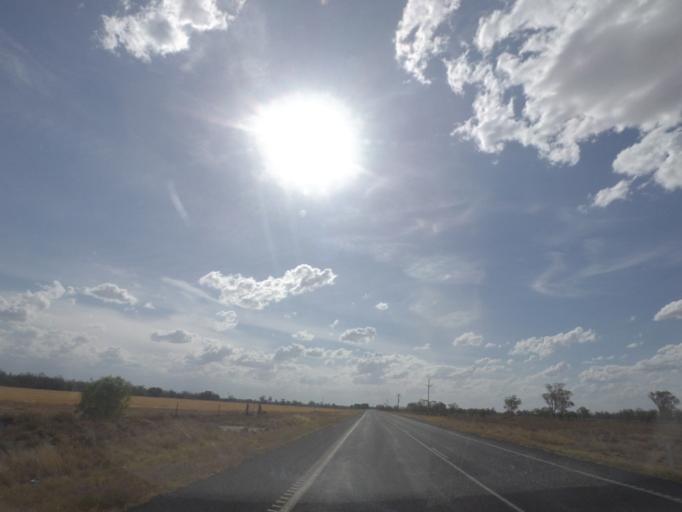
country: AU
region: New South Wales
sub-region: Moree Plains
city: Boggabilla
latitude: -28.5828
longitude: 150.8085
